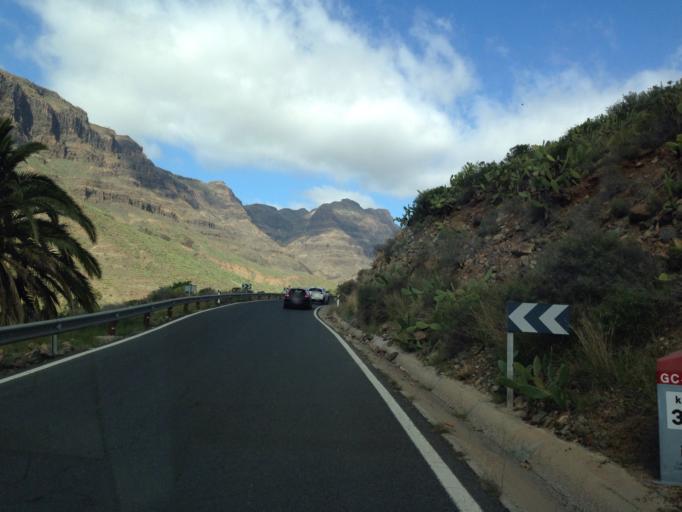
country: ES
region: Canary Islands
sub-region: Provincia de Las Palmas
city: Santa Lucia
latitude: 27.8525
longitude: -15.5654
